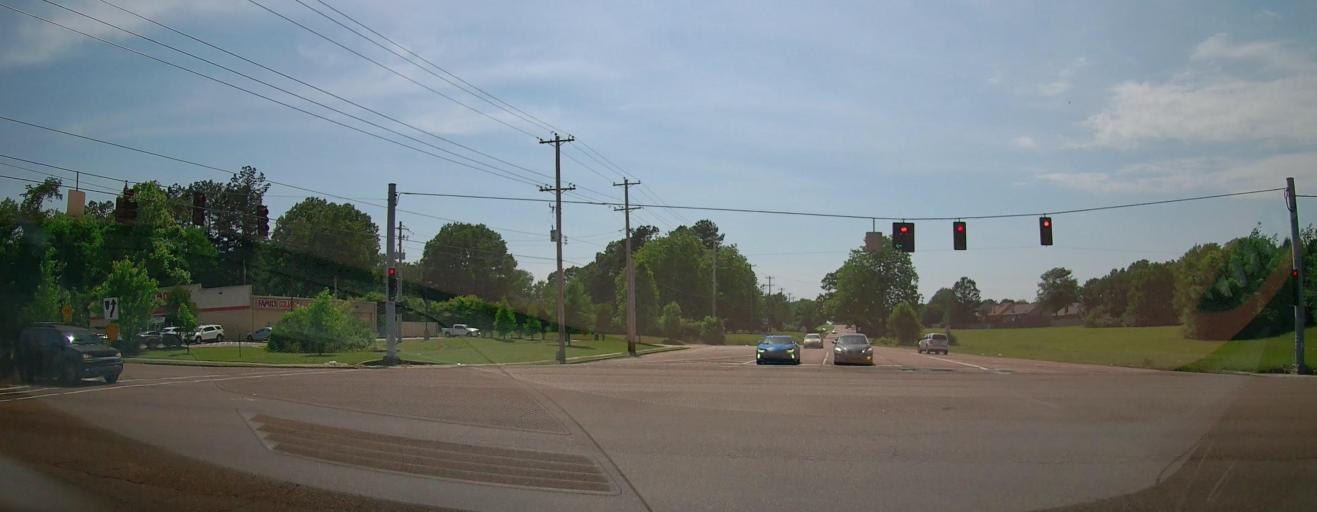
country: US
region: Mississippi
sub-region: De Soto County
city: Olive Branch
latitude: 35.0058
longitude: -89.8310
